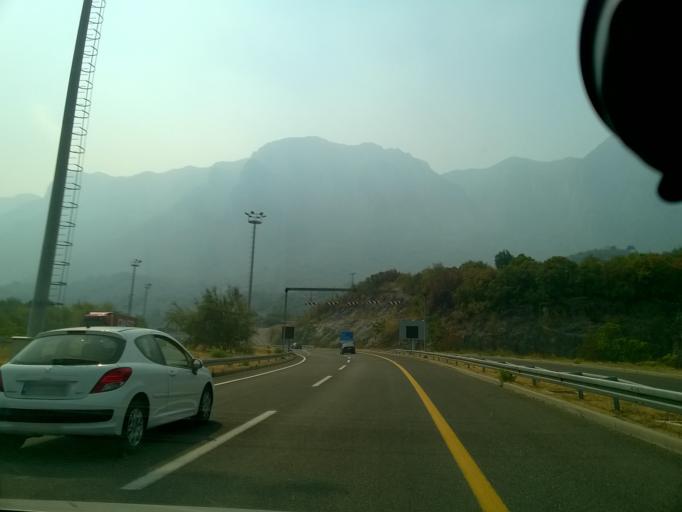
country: ME
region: Bar
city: Sutomore
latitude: 42.2028
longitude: 19.0505
